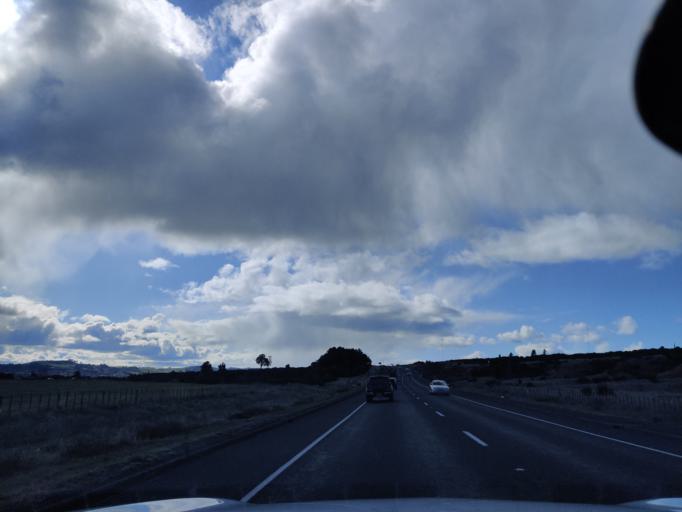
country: NZ
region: Waikato
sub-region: Taupo District
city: Taupo
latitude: -38.7480
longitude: 176.0737
